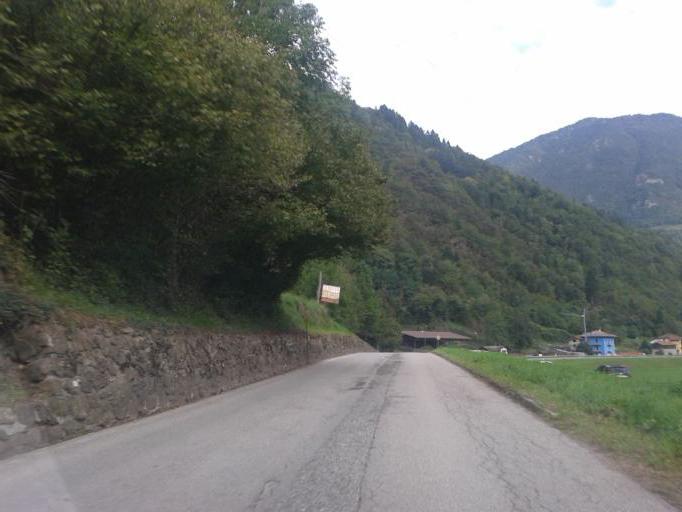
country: IT
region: Trentino-Alto Adige
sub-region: Provincia di Trento
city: Cimego
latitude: 45.9006
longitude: 10.6081
